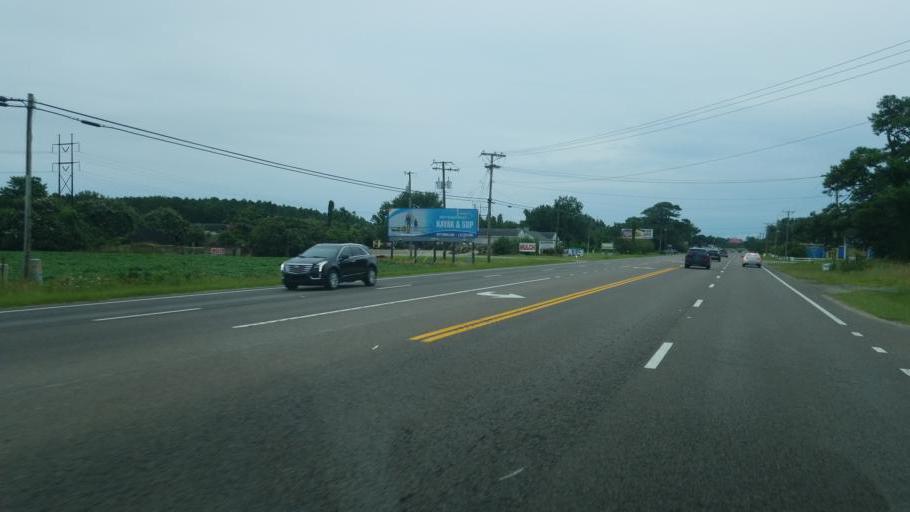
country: US
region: North Carolina
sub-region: Dare County
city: Southern Shores
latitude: 36.1703
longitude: -75.8607
